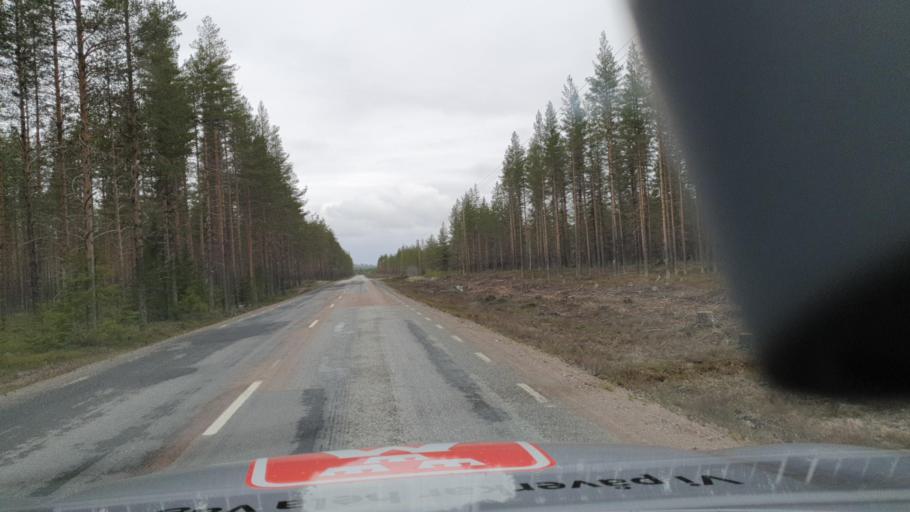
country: SE
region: Vaesternorrland
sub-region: Solleftea Kommun
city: Solleftea
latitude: 63.6158
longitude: 17.4918
